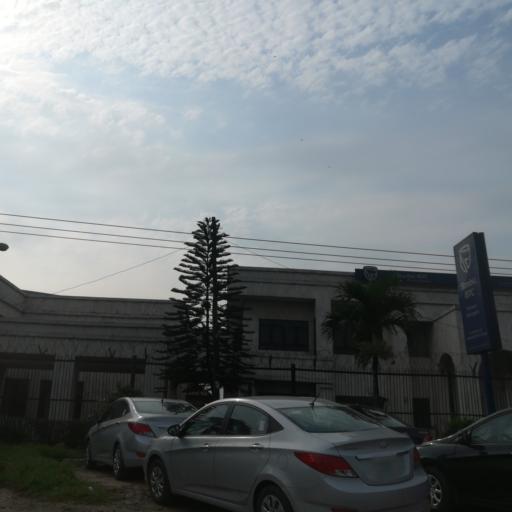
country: NG
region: Rivers
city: Port Harcourt
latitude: 4.8493
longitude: 7.0516
